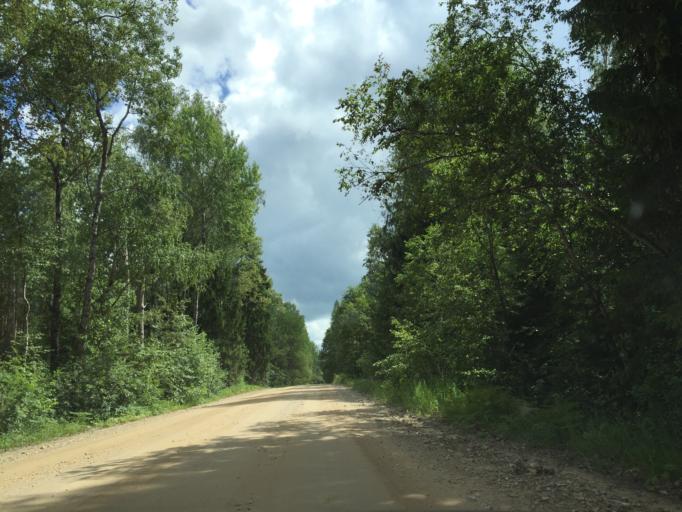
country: LV
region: Ropazu
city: Ropazi
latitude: 56.9176
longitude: 24.7428
